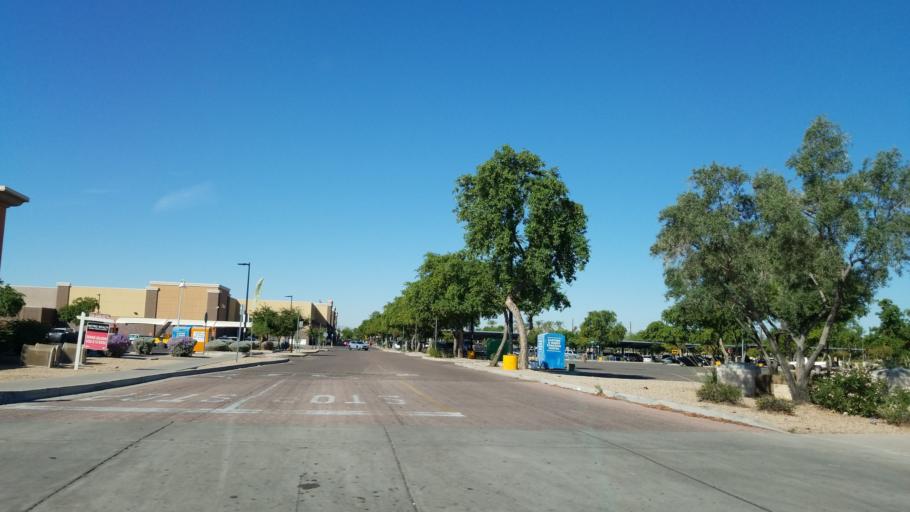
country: US
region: Arizona
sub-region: Maricopa County
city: Glendale
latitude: 33.5518
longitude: -112.1776
